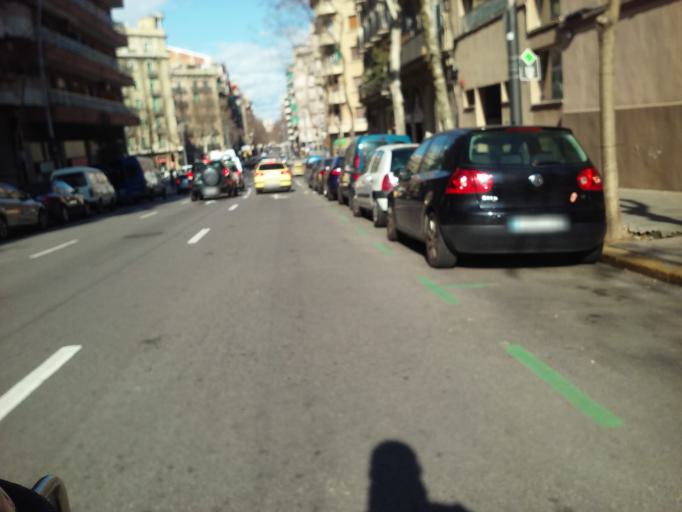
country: ES
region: Catalonia
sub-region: Provincia de Barcelona
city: Sants-Montjuic
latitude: 41.3741
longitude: 2.1552
